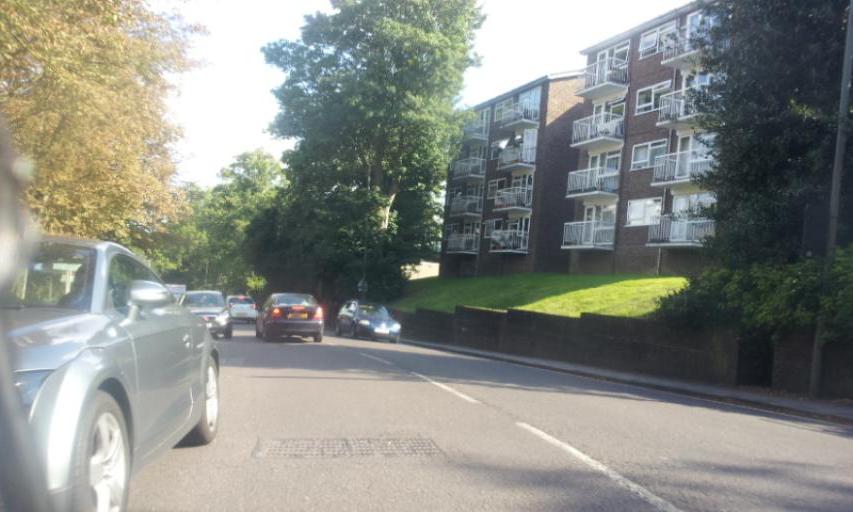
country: GB
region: England
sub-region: Greater London
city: Bromley
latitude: 51.4070
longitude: -0.0023
